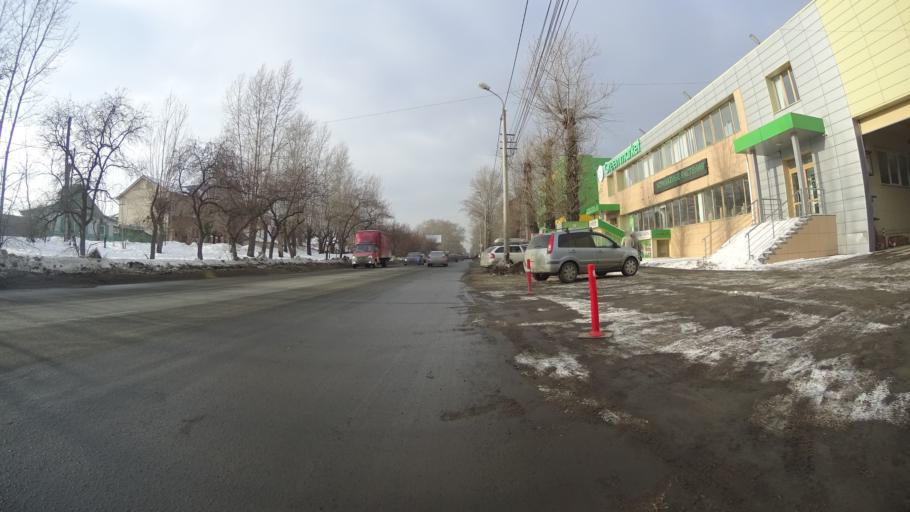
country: RU
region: Chelyabinsk
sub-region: Gorod Chelyabinsk
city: Chelyabinsk
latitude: 55.1204
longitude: 61.3802
